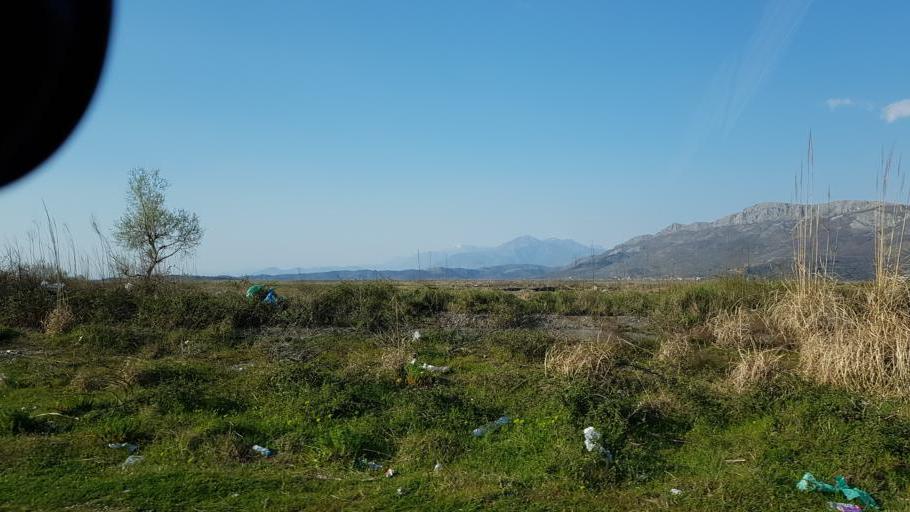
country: AL
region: Shkoder
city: Vukatane
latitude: 41.9911
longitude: 19.5671
